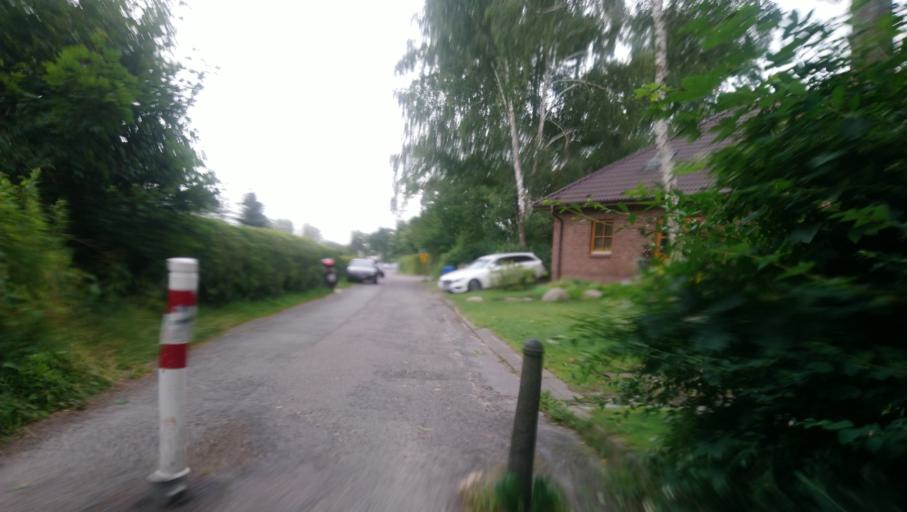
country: DE
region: Mecklenburg-Vorpommern
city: Rostock
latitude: 54.0679
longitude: 12.1006
